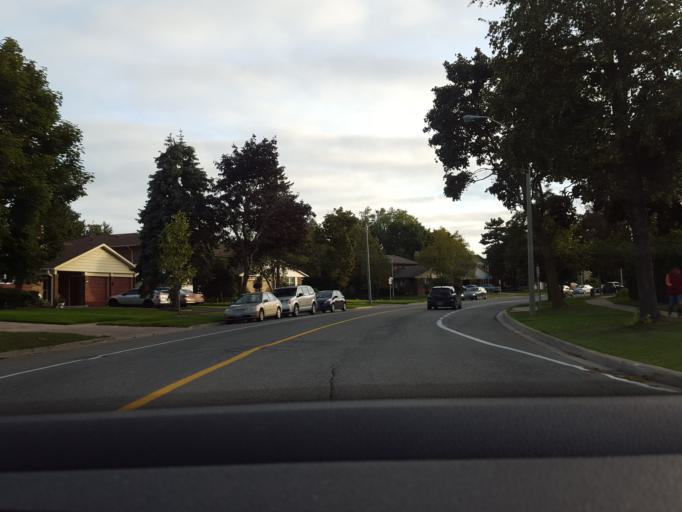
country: CA
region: Ontario
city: Scarborough
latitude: 43.7870
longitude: -79.3080
